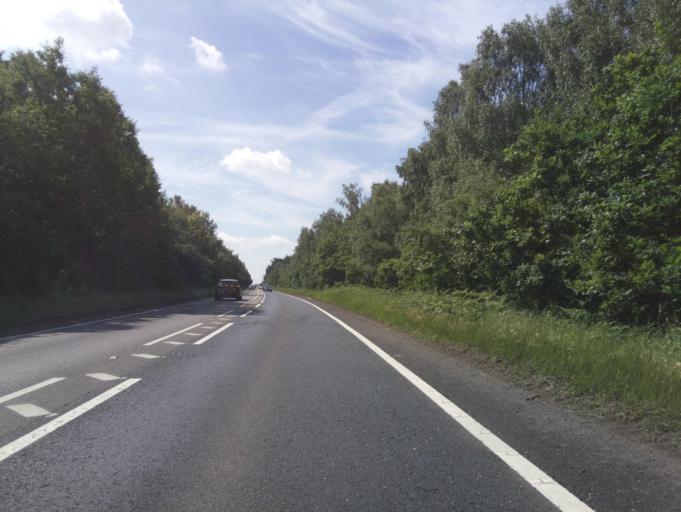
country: GB
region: England
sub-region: Lincolnshire
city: Skellingthorpe
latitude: 53.2160
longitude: -0.6178
